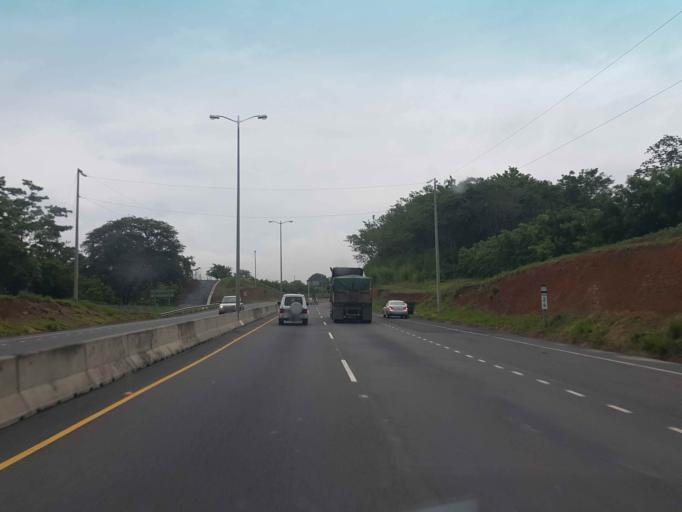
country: CR
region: Alajuela
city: Atenas
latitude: 9.9654
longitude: -84.3122
